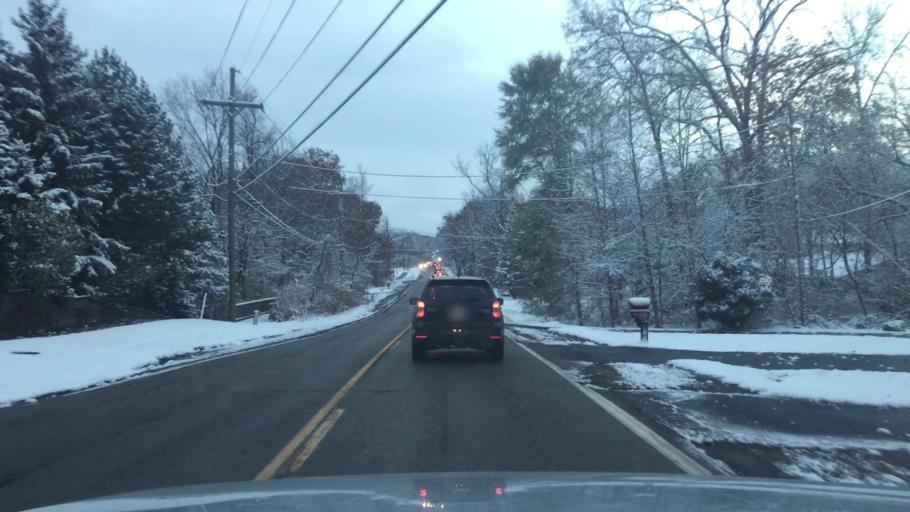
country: US
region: Michigan
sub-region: Oakland County
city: West Bloomfield Township
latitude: 42.6026
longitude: -83.3980
